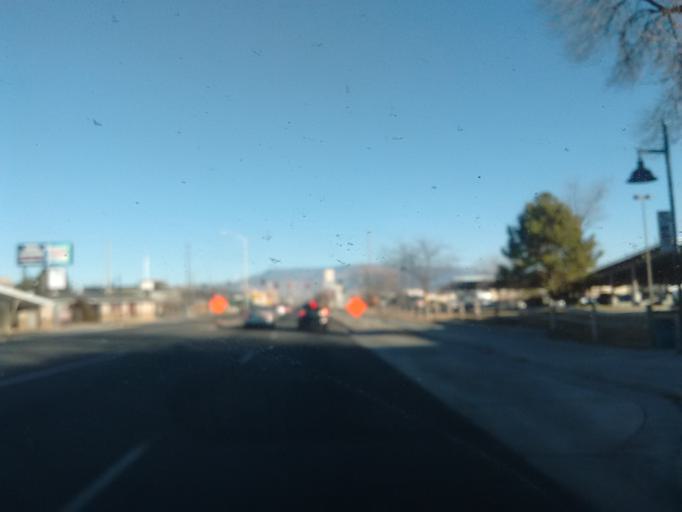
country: US
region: Colorado
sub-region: Mesa County
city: Grand Junction
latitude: 39.0773
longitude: -108.5398
